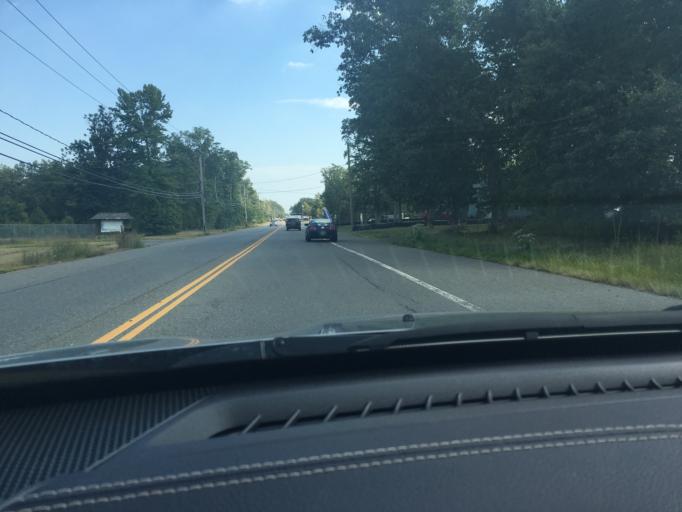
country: US
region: New Jersey
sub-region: Ocean County
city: Leisure Knoll
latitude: 40.0260
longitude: -74.2739
